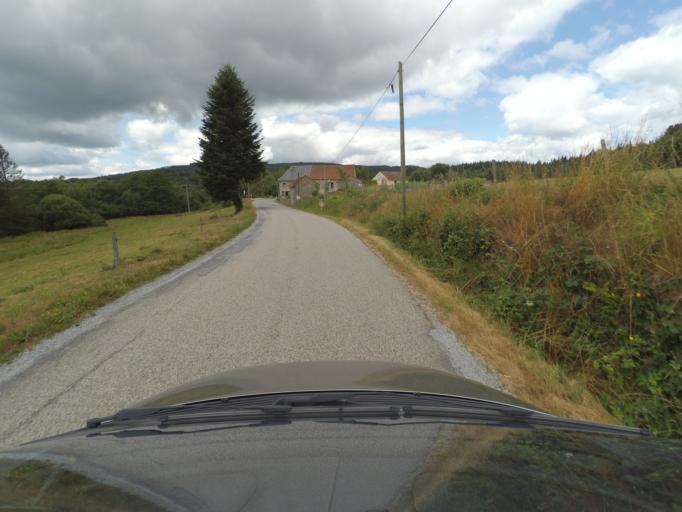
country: FR
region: Limousin
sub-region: Departement de la Haute-Vienne
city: Peyrat-le-Chateau
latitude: 45.8217
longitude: 1.9201
